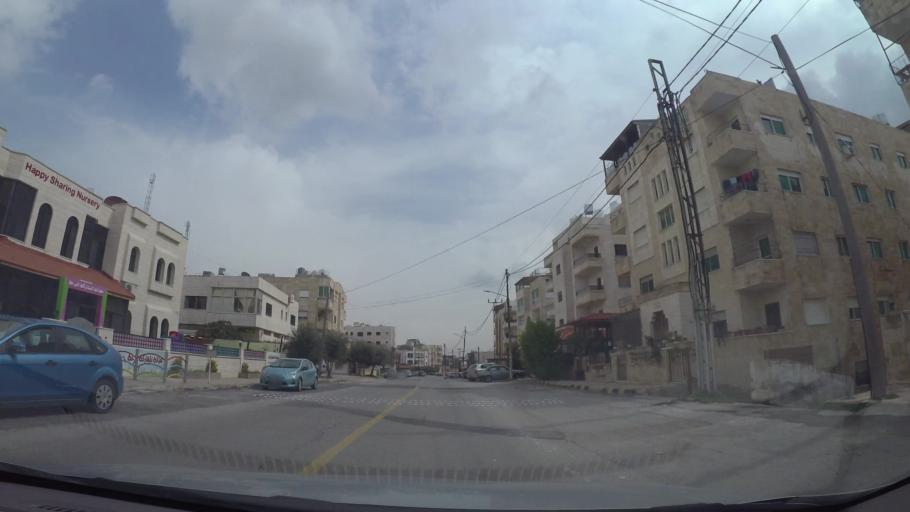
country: JO
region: Amman
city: Umm as Summaq
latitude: 31.8969
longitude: 35.8358
